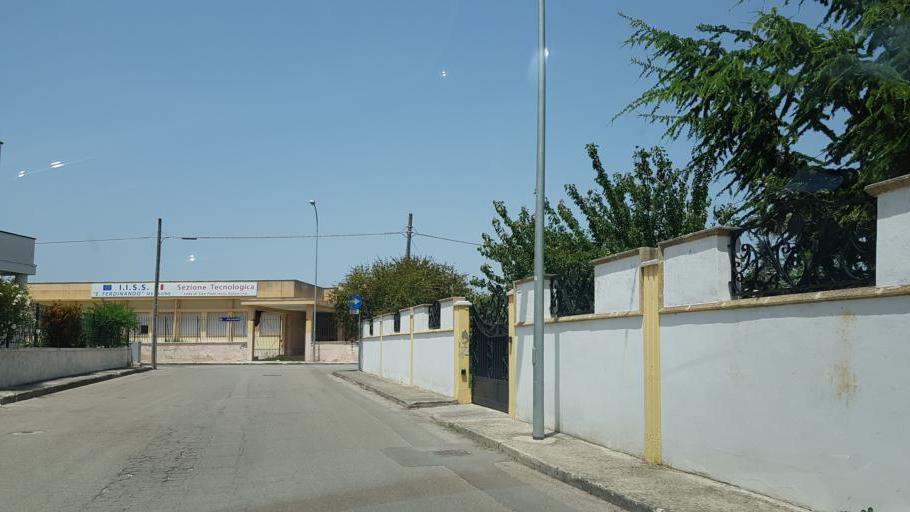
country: IT
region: Apulia
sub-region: Provincia di Brindisi
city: San Pancrazio Salentino
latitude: 40.4225
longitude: 17.8465
